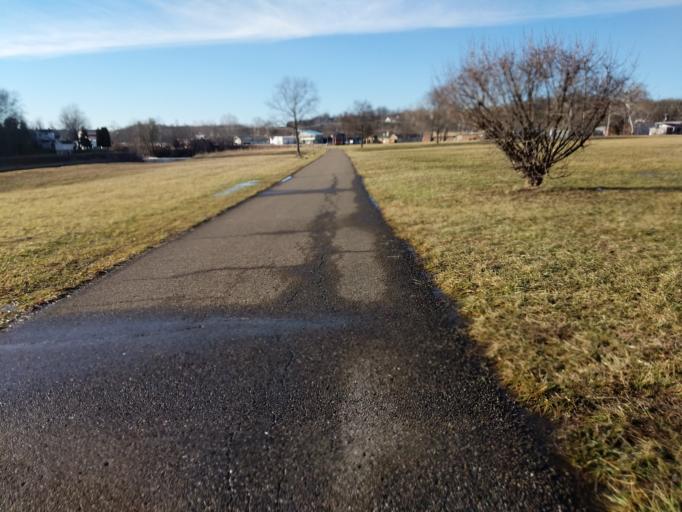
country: US
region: Ohio
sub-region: Athens County
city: Athens
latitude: 39.3290
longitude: -82.1205
